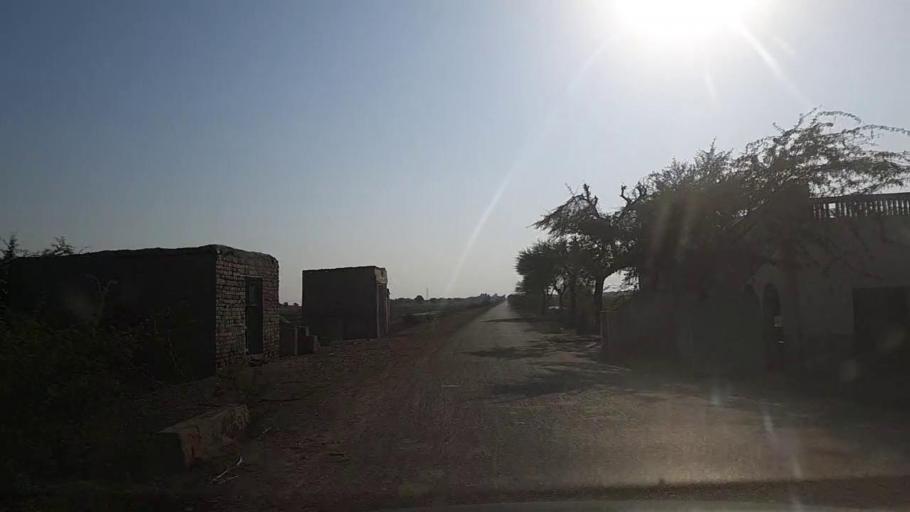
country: PK
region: Sindh
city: Naukot
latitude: 25.0052
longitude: 69.2734
